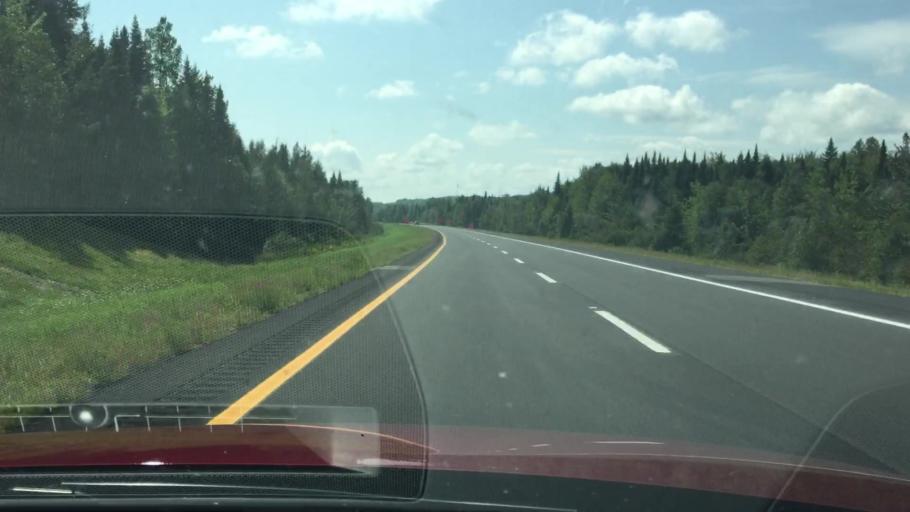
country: US
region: Maine
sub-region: Penobscot County
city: Patten
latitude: 45.8951
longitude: -68.3984
